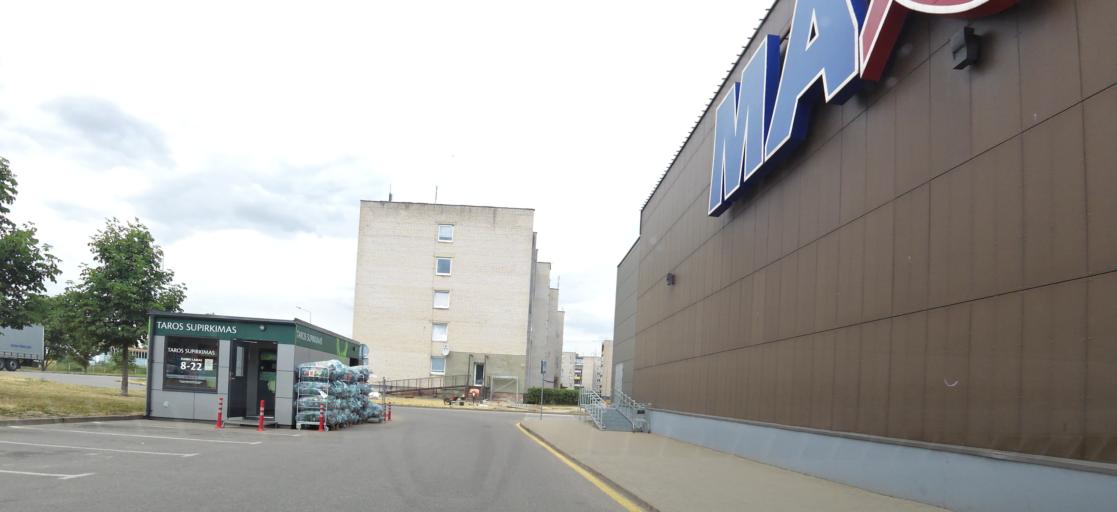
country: LT
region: Vilnius County
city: Ukmerge
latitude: 55.2428
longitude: 24.7437
